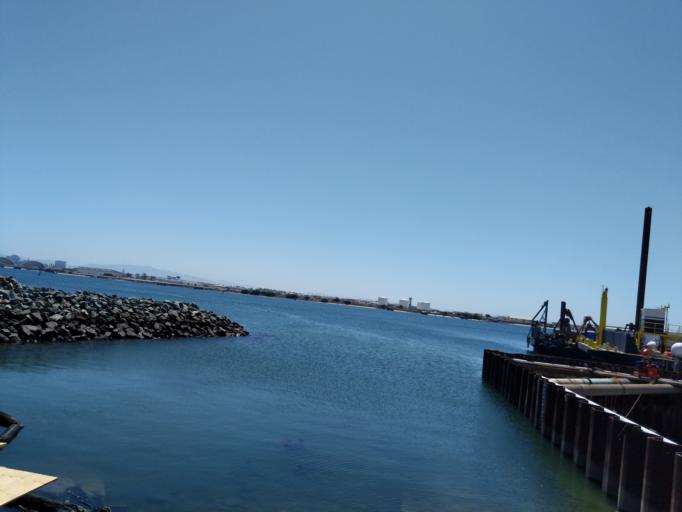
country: US
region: California
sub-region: San Diego County
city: Coronado
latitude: 32.7158
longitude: -117.2233
